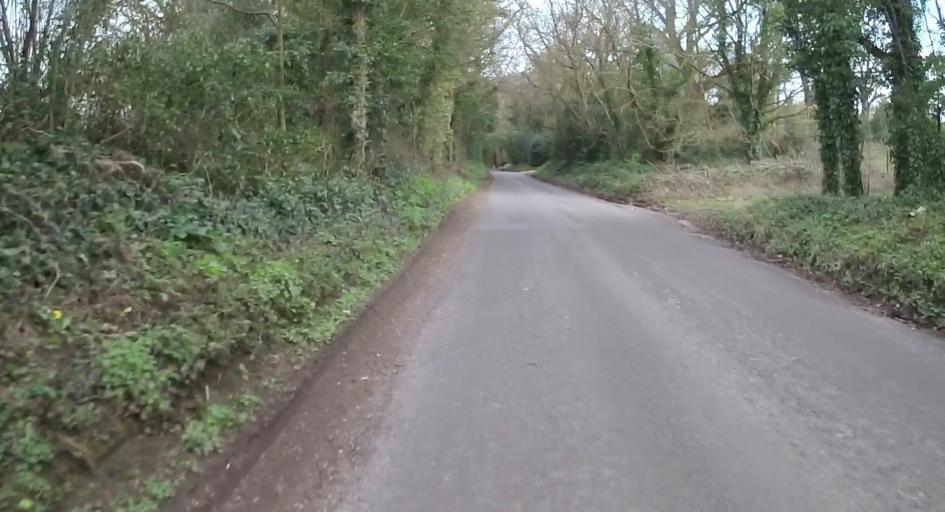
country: GB
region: England
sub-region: Hampshire
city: Andover
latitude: 51.1545
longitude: -1.4678
